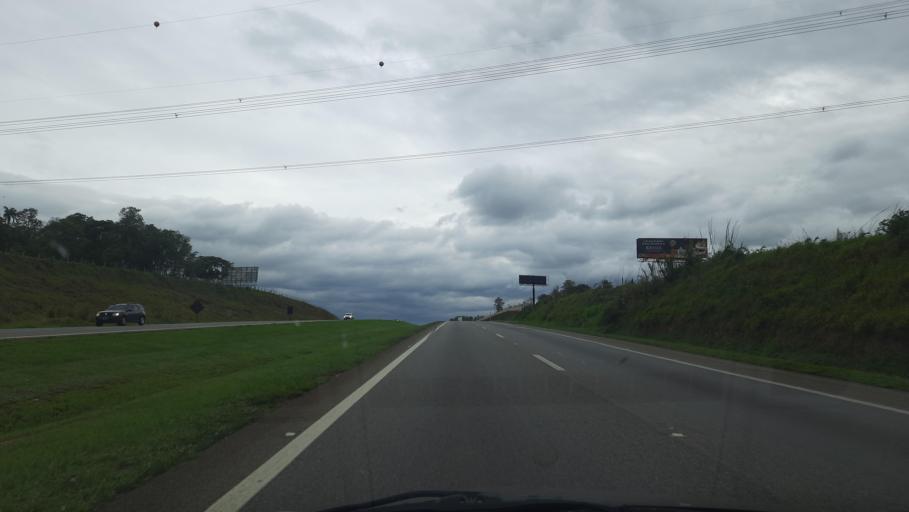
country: BR
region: Sao Paulo
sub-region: Jaguariuna
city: Jaguariuna
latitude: -22.7412
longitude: -47.0189
